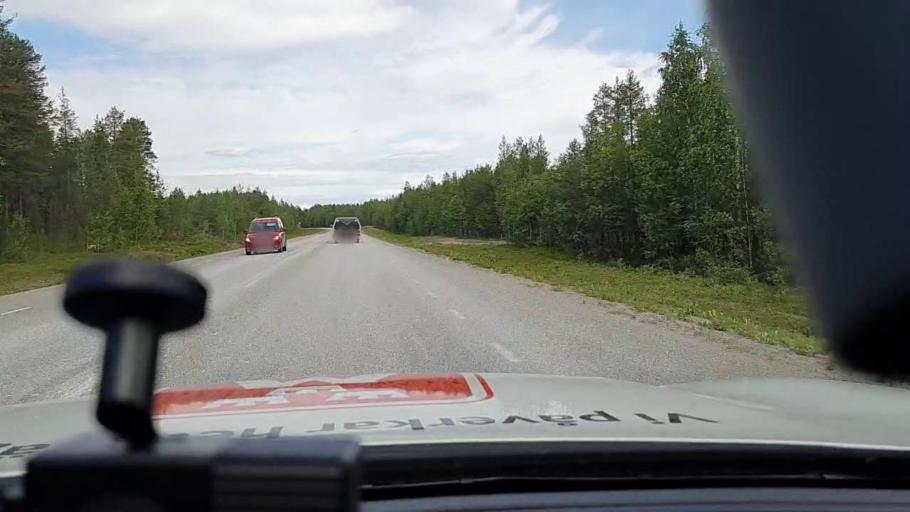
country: SE
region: Norrbotten
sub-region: Jokkmokks Kommun
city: Jokkmokk
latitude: 66.5060
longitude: 20.2491
